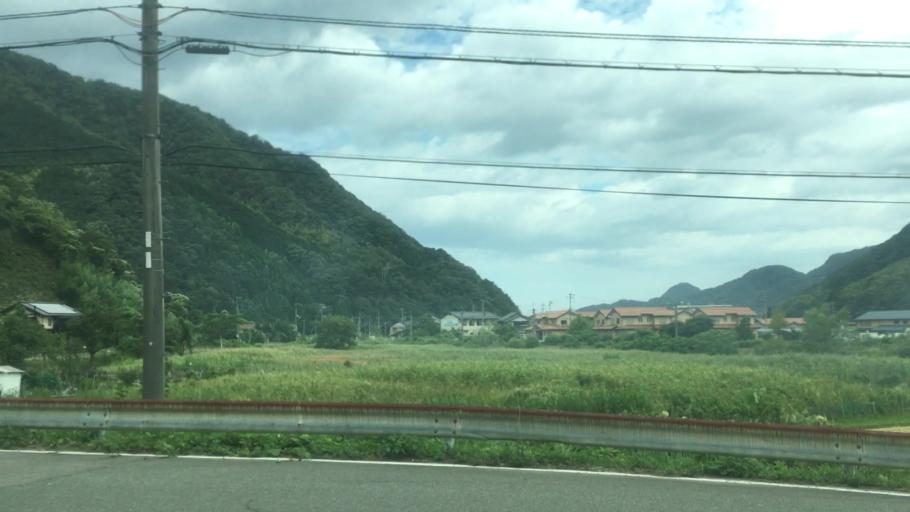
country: JP
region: Hyogo
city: Toyooka
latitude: 35.6042
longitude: 134.8002
